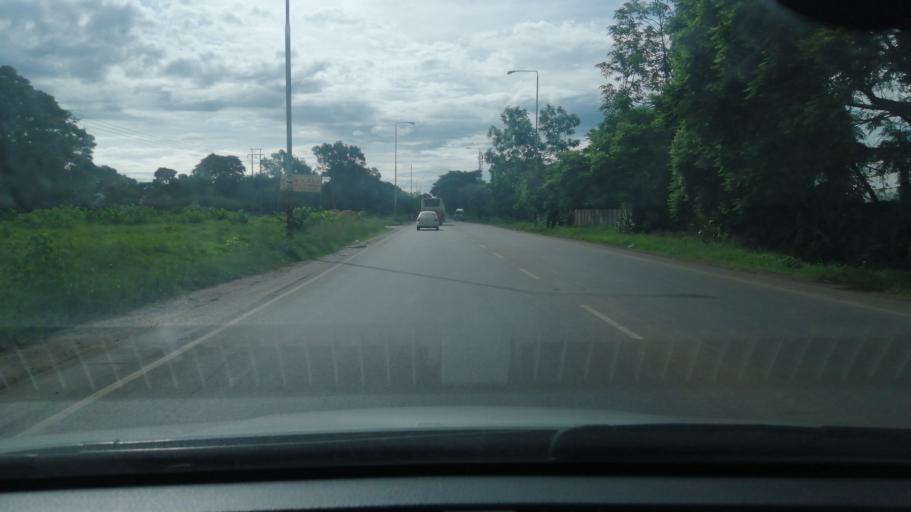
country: ZW
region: Harare
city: Harare
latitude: -17.7641
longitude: 30.9921
